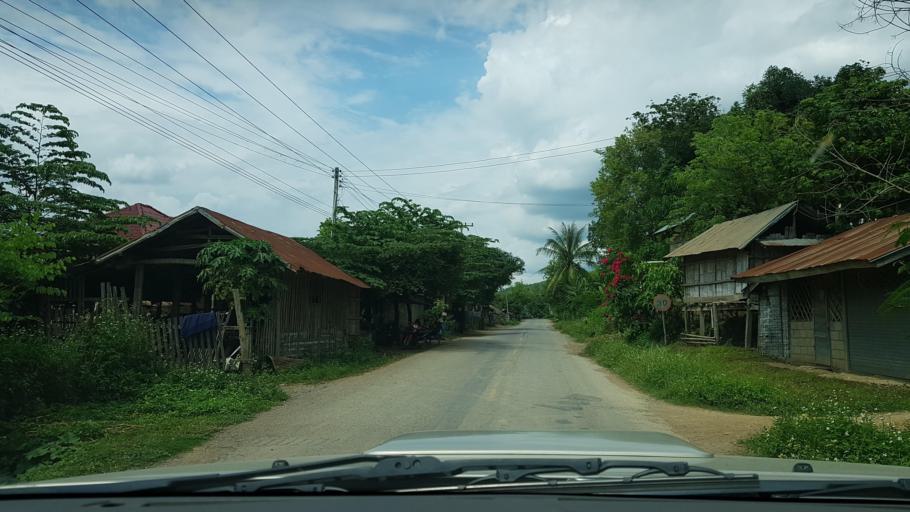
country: LA
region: Loungnamtha
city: Muang Nale
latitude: 20.2509
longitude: 101.5830
